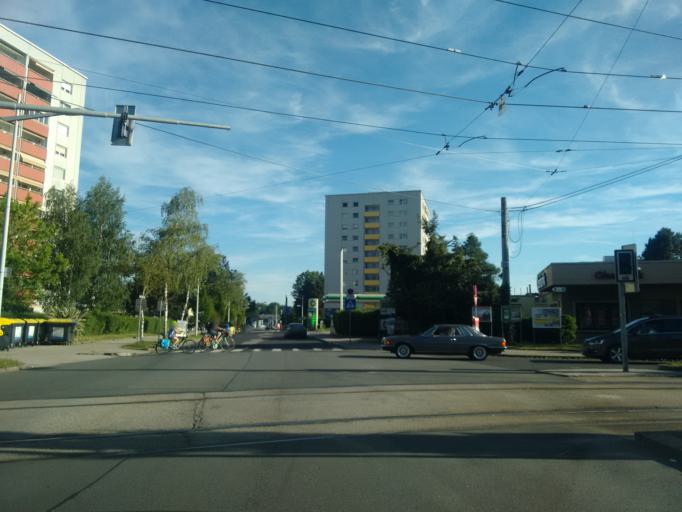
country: AT
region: Upper Austria
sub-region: Linz Stadt
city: Linz
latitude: 48.3321
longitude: 14.3177
